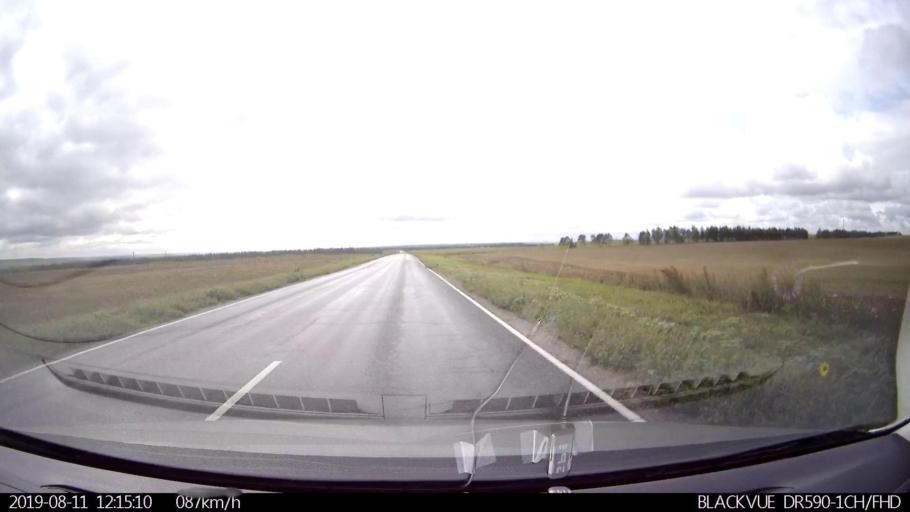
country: RU
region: Ulyanovsk
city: Ignatovka
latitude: 53.9446
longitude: 47.9705
